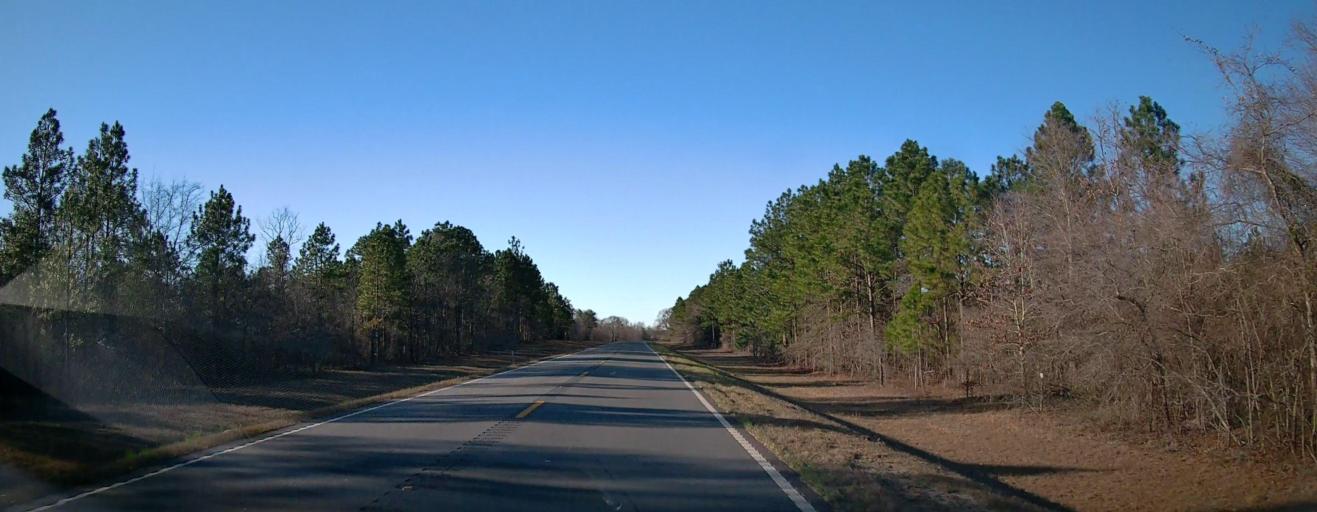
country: US
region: Georgia
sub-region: Talbot County
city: Talbotton
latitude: 32.5290
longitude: -84.4321
